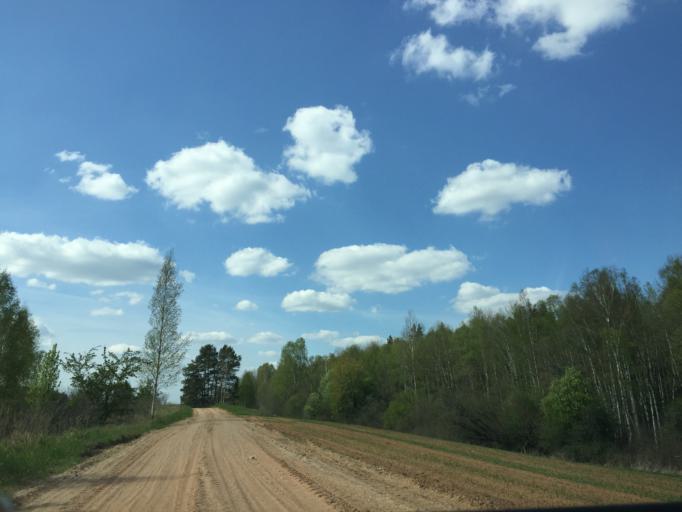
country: LV
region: Vecumnieki
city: Vecumnieki
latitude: 56.4795
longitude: 24.5696
